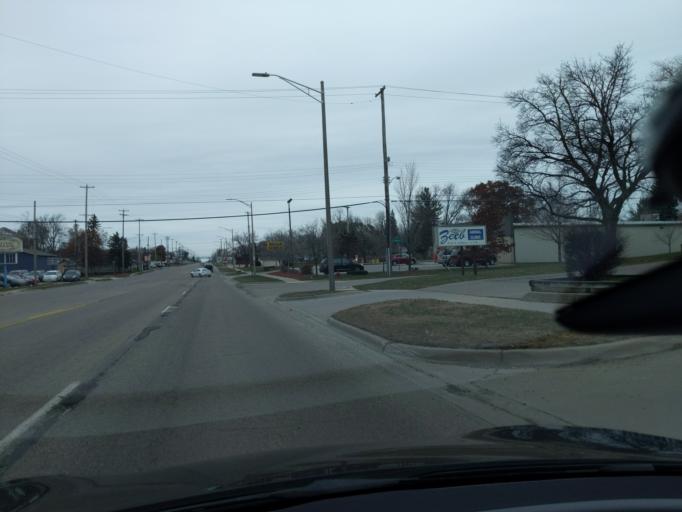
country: US
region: Michigan
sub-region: Ingham County
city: Lansing
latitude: 42.7635
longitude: -84.5427
